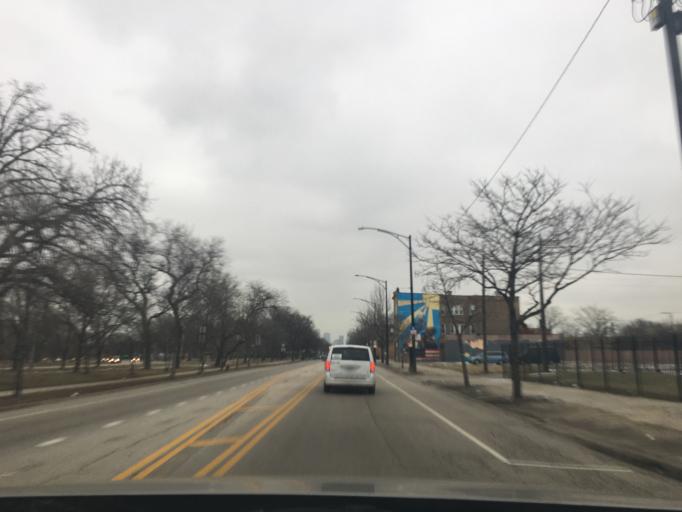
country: US
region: Illinois
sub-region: Cook County
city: Cicero
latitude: 41.8809
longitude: -87.7156
